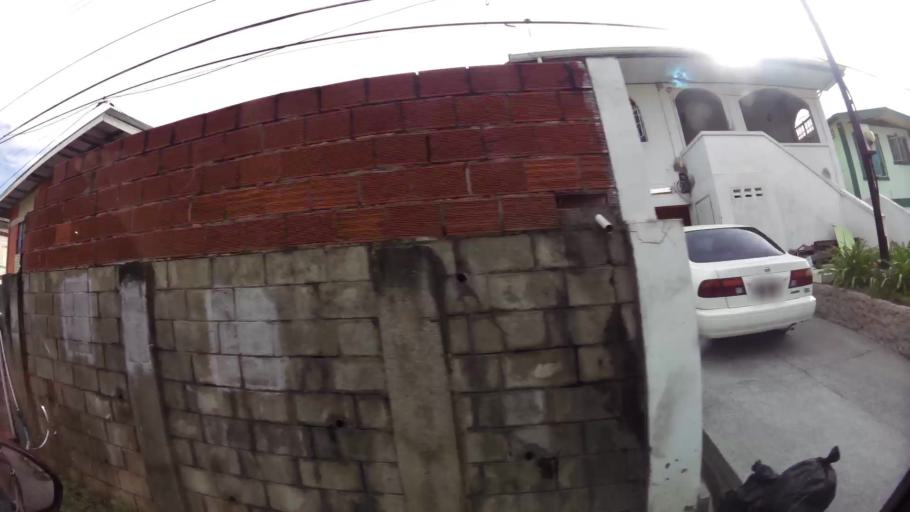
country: TT
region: San Juan/Laventille
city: Laventille
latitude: 10.6517
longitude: -61.4441
